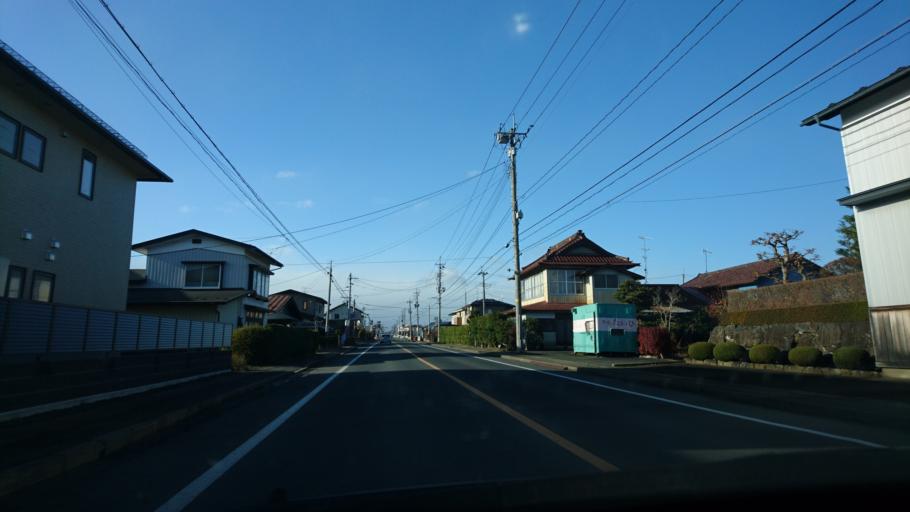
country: JP
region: Iwate
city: Mizusawa
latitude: 39.1274
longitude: 141.1593
